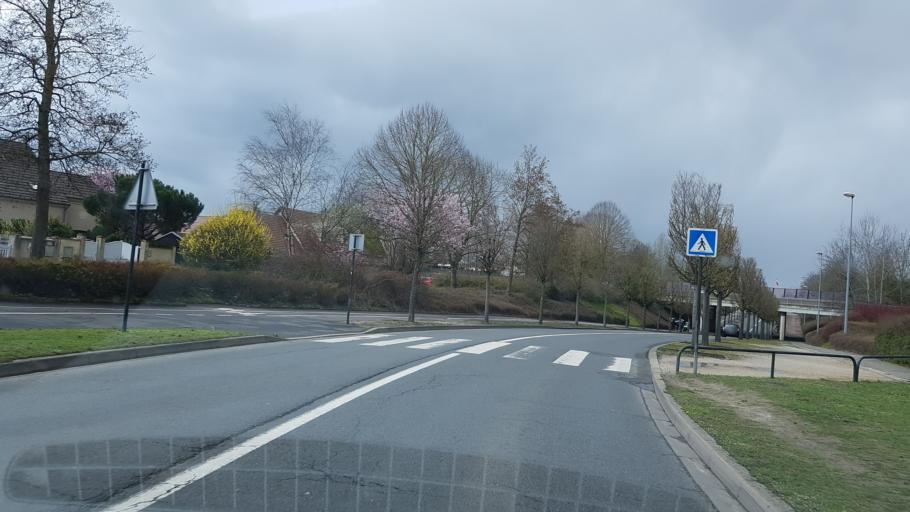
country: FR
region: Ile-de-France
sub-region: Departement des Yvelines
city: Rambouillet
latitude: 48.6441
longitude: 1.8433
